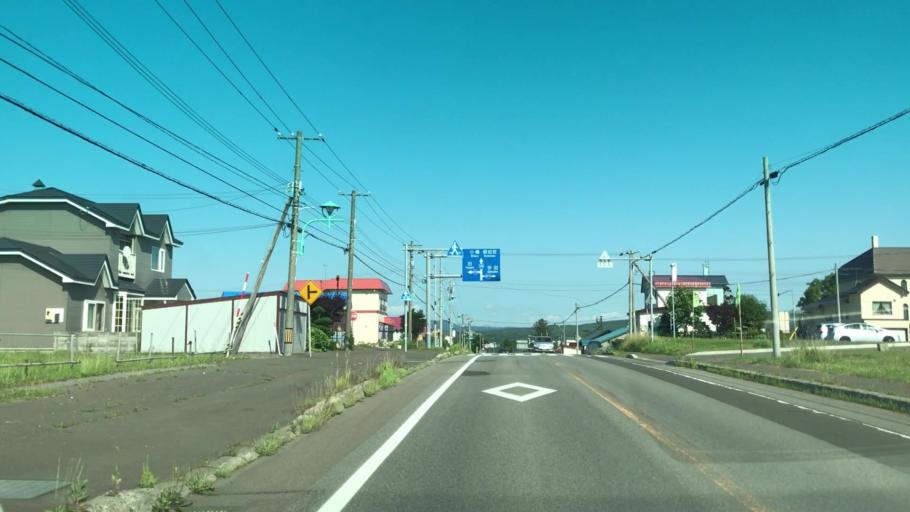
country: JP
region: Hokkaido
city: Iwanai
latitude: 42.9818
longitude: 140.5715
